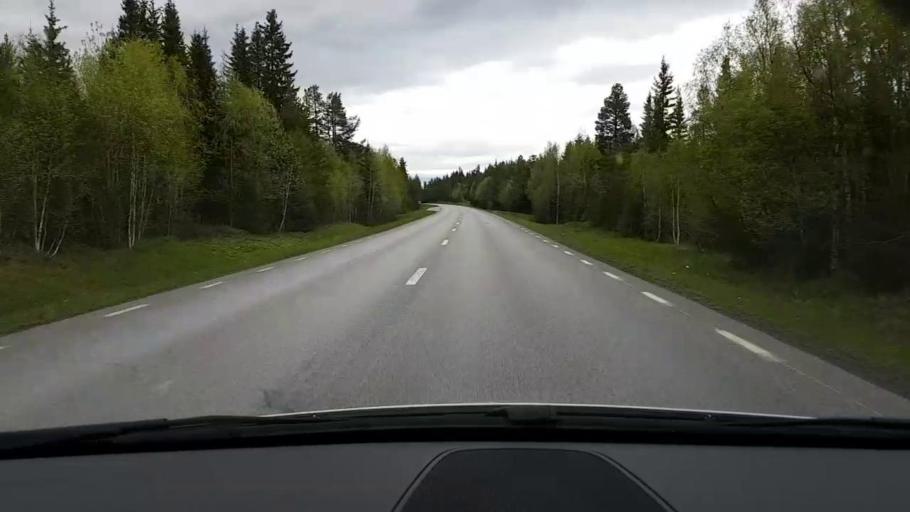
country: SE
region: Jaemtland
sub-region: Krokoms Kommun
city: Valla
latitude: 63.2958
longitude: 13.9269
